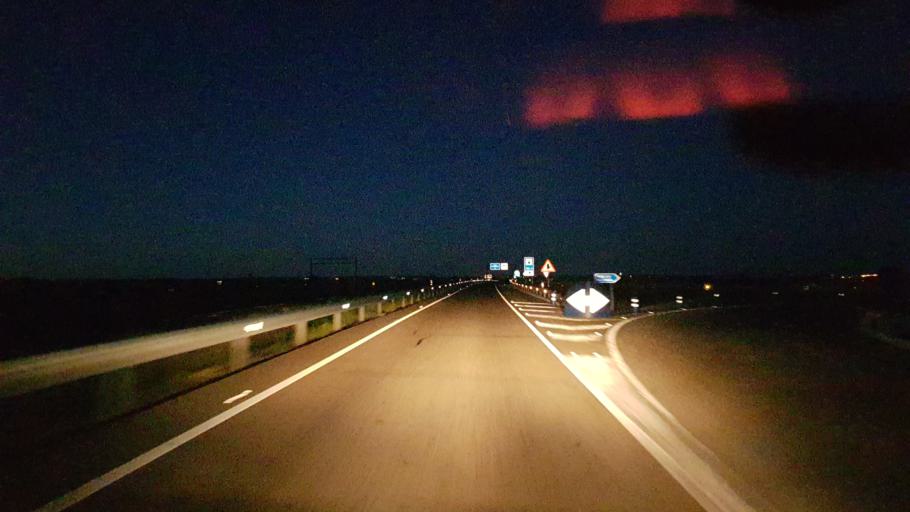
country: ES
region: Castille and Leon
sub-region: Provincia de Zamora
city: Monfarracinos
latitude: 41.5318
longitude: -5.7046
